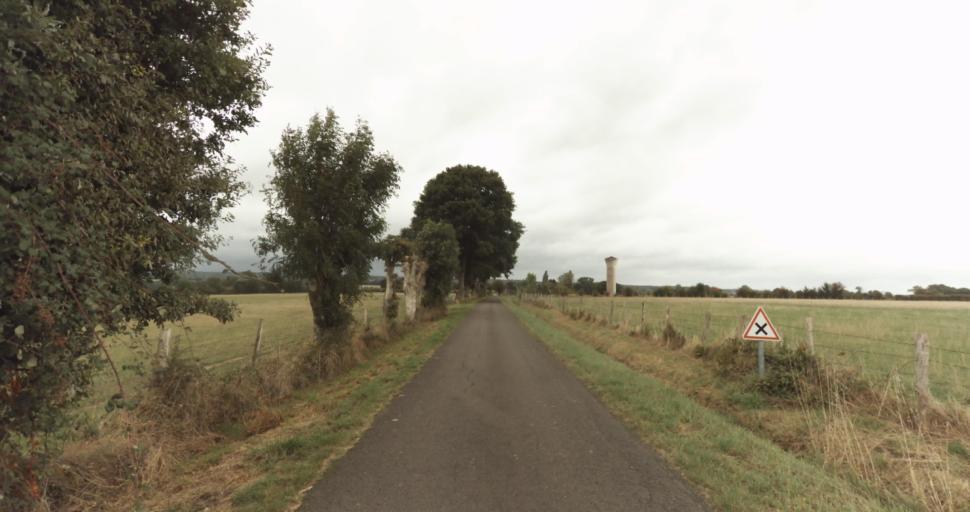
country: FR
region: Lower Normandy
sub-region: Departement de l'Orne
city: Sainte-Gauburge-Sainte-Colombe
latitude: 48.7220
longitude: 0.4882
